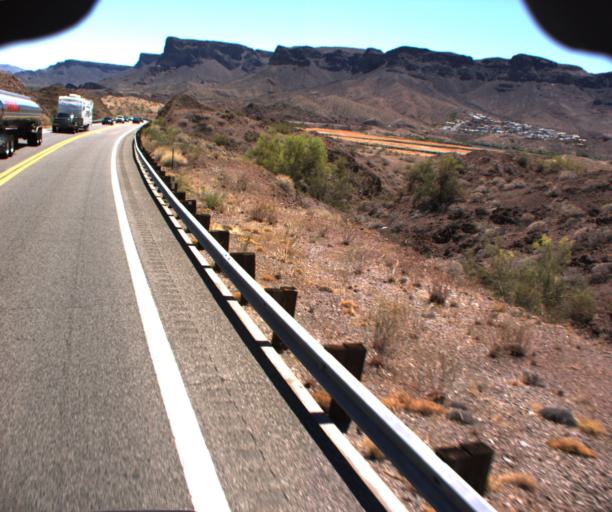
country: US
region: Arizona
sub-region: La Paz County
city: Cienega Springs
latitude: 34.3081
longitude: -114.1001
